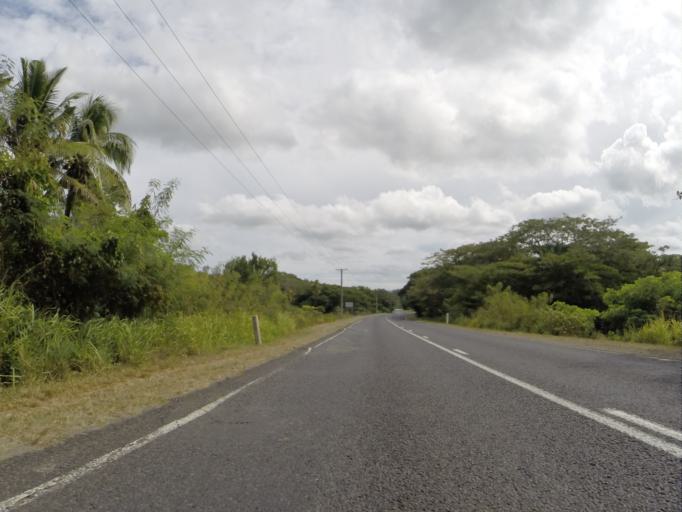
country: FJ
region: Western
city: Nadi
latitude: -18.0859
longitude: 177.3788
